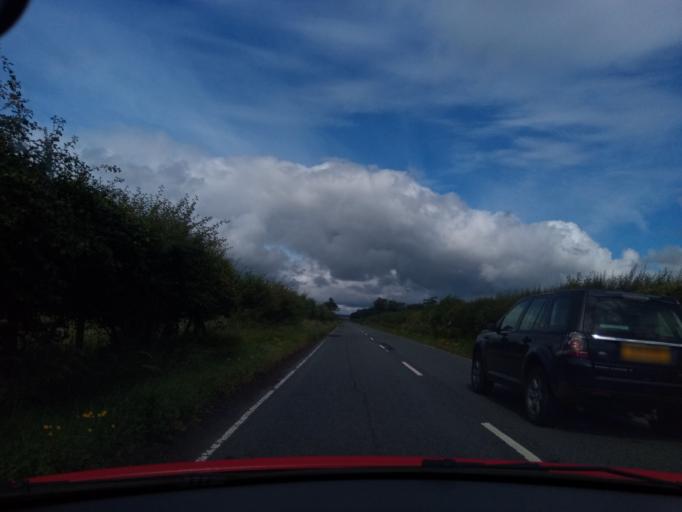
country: GB
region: Scotland
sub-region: The Scottish Borders
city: Lauder
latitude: 55.7295
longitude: -2.7291
